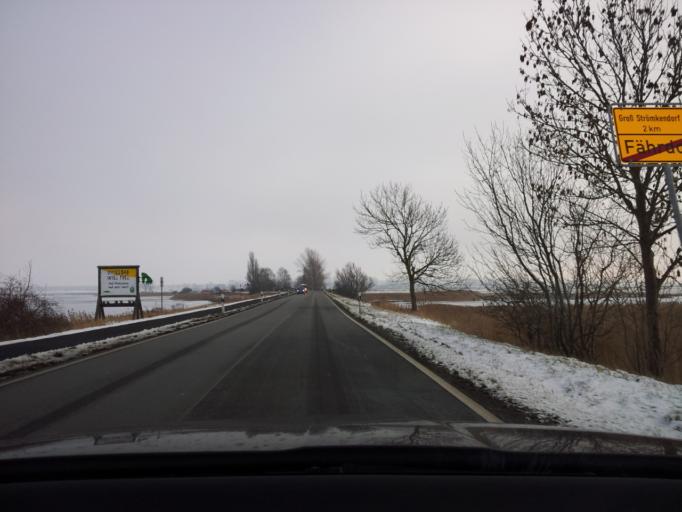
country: DE
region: Mecklenburg-Vorpommern
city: Blowatz
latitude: 53.9724
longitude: 11.4669
